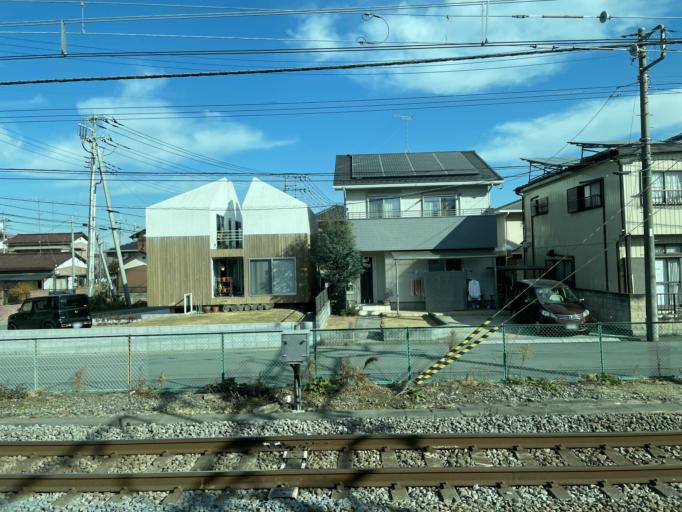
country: JP
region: Saitama
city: Fukayacho
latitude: 36.1725
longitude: 139.3345
